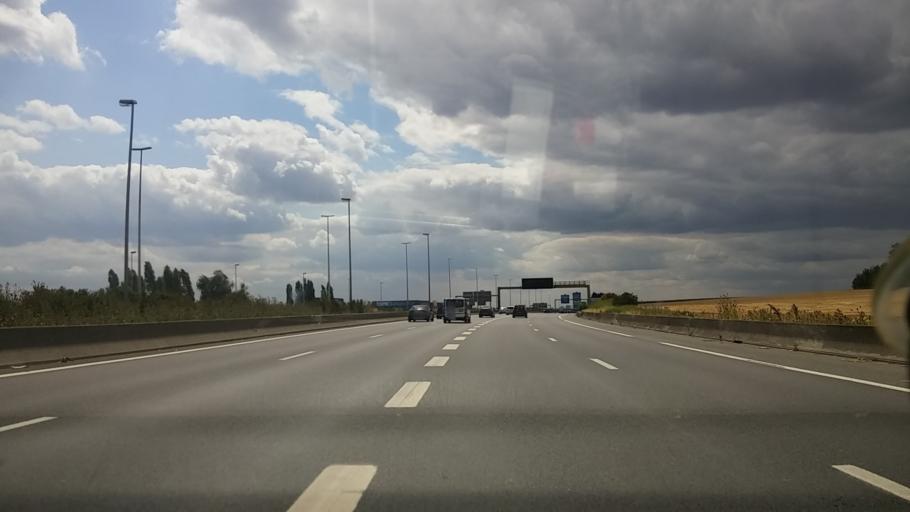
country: FR
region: Ile-de-France
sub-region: Departement du Val-d'Oise
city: Roissy-en-France
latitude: 48.9833
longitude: 2.5013
